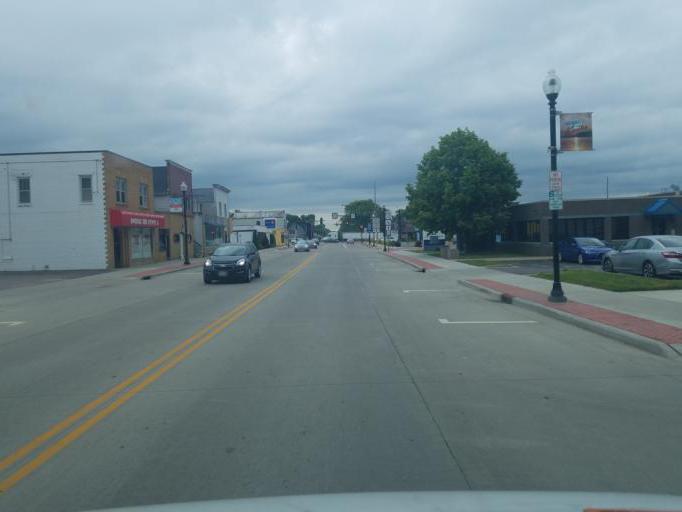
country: US
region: Wisconsin
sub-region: Juneau County
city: Mauston
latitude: 43.7962
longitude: -90.0740
